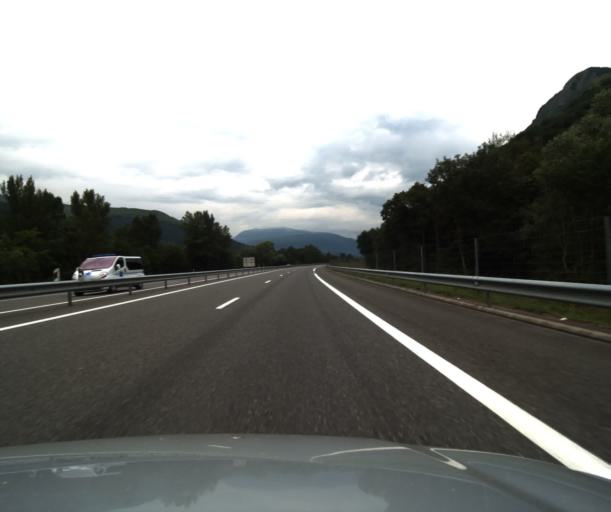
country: FR
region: Midi-Pyrenees
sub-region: Departement des Hautes-Pyrenees
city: Lourdes
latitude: 43.0595
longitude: -0.0438
